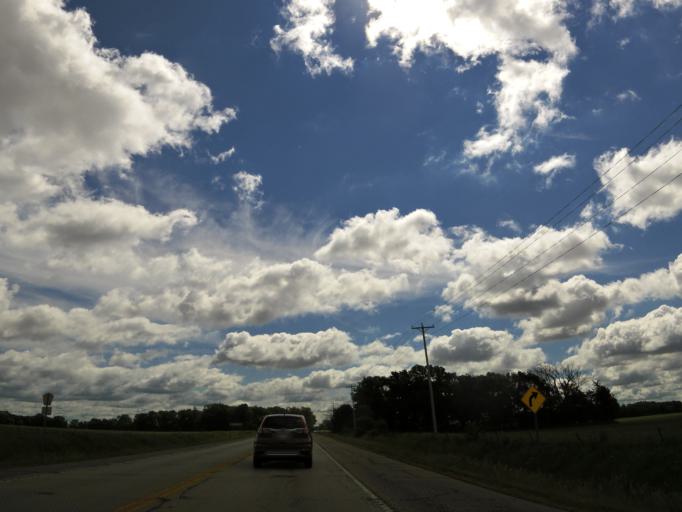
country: US
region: Minnesota
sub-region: Fillmore County
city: Spring Valley
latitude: 43.7111
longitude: -92.4269
